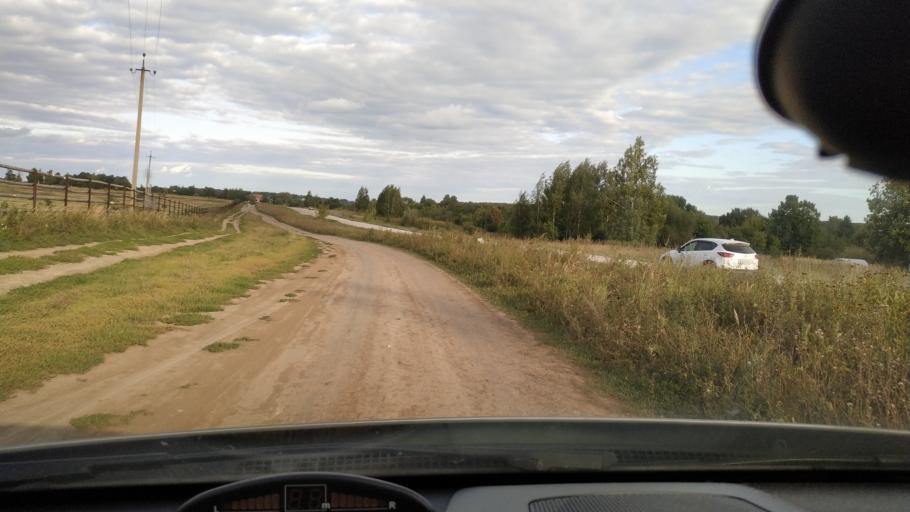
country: RU
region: Rjazan
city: Polyany
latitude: 54.5650
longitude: 39.8660
